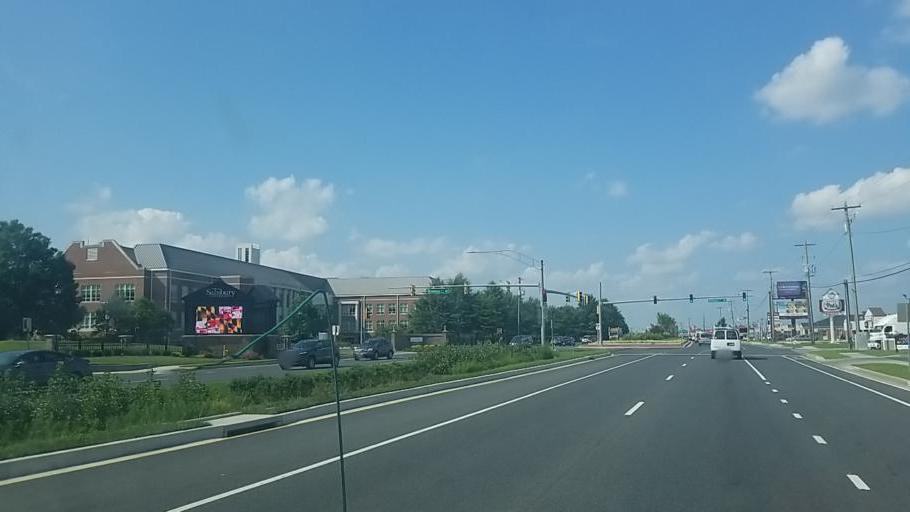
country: US
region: Maryland
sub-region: Wicomico County
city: Salisbury
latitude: 38.3437
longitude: -75.6041
